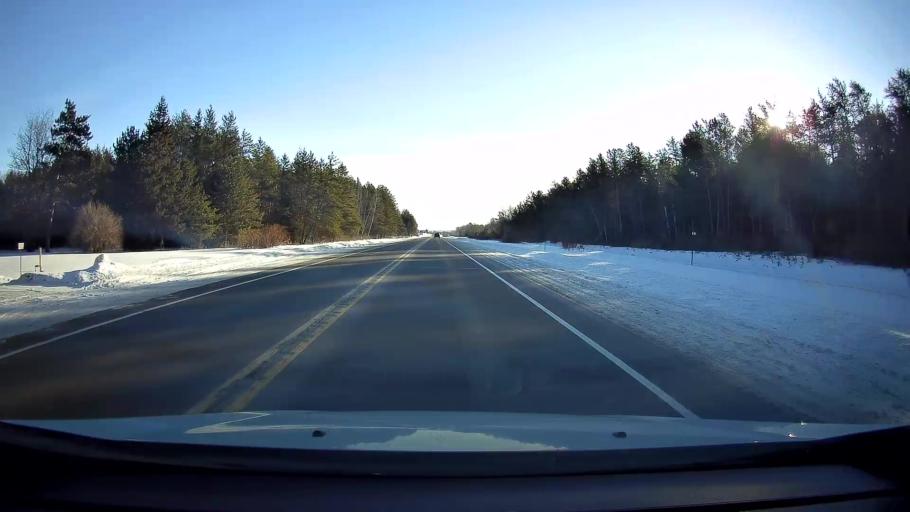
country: US
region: Wisconsin
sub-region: Sawyer County
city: Hayward
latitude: 45.9843
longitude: -91.5770
